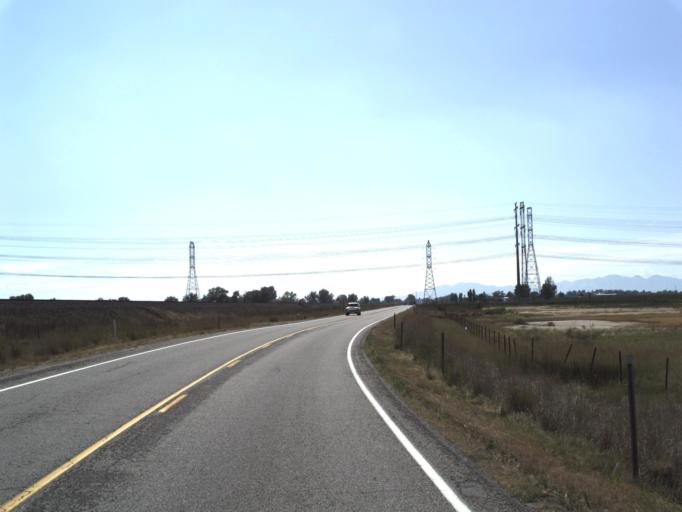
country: US
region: Utah
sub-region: Weber County
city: Marriott-Slaterville
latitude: 41.2445
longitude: -112.0485
